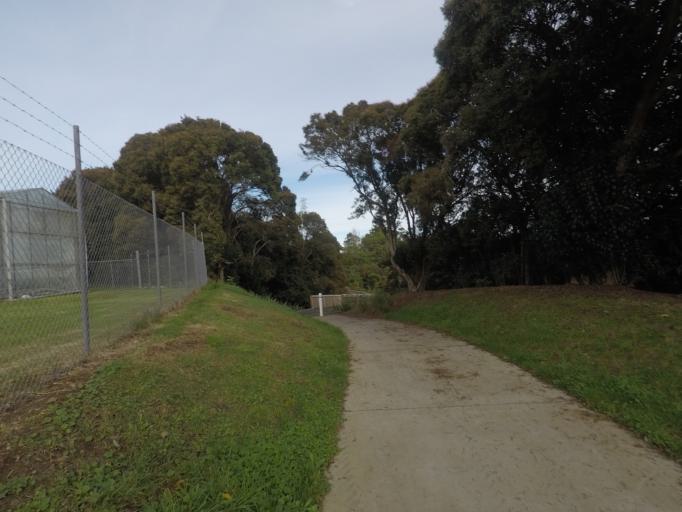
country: NZ
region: Auckland
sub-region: Auckland
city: Mangere
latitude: -36.9479
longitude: 174.8042
